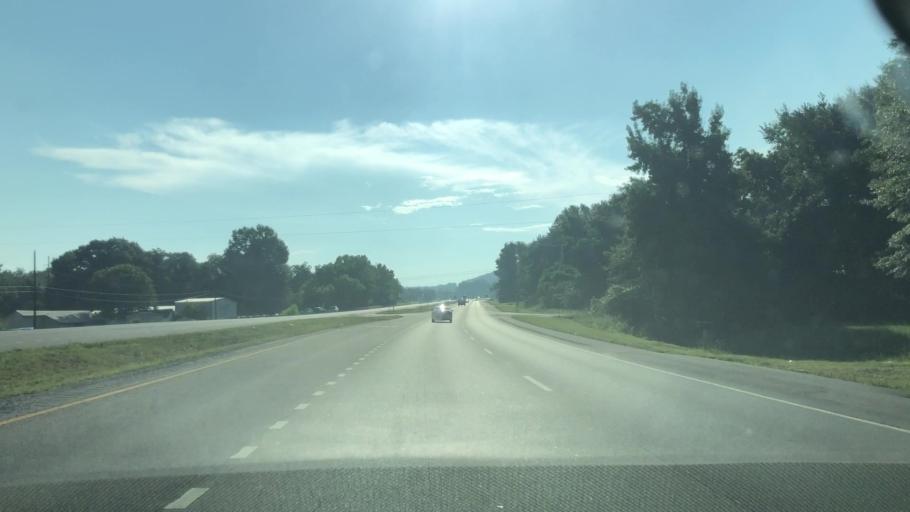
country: US
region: Alabama
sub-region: Calhoun County
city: West End-Cobb Town
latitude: 33.6472
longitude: -85.8721
